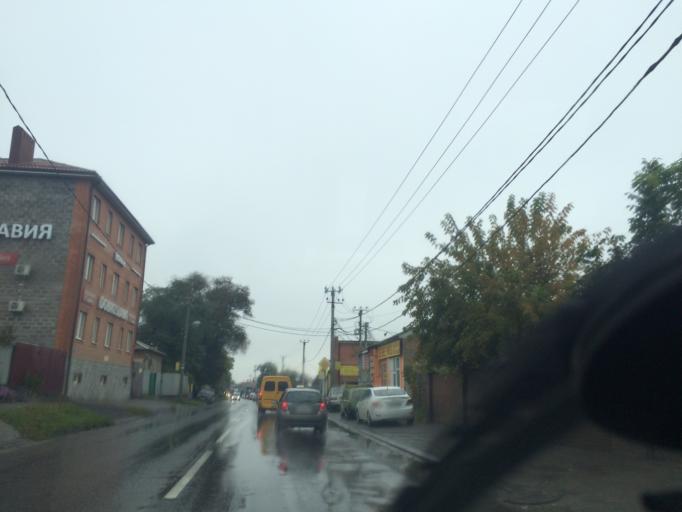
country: RU
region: Rostov
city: Rostov-na-Donu
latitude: 47.1911
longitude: 39.6241
